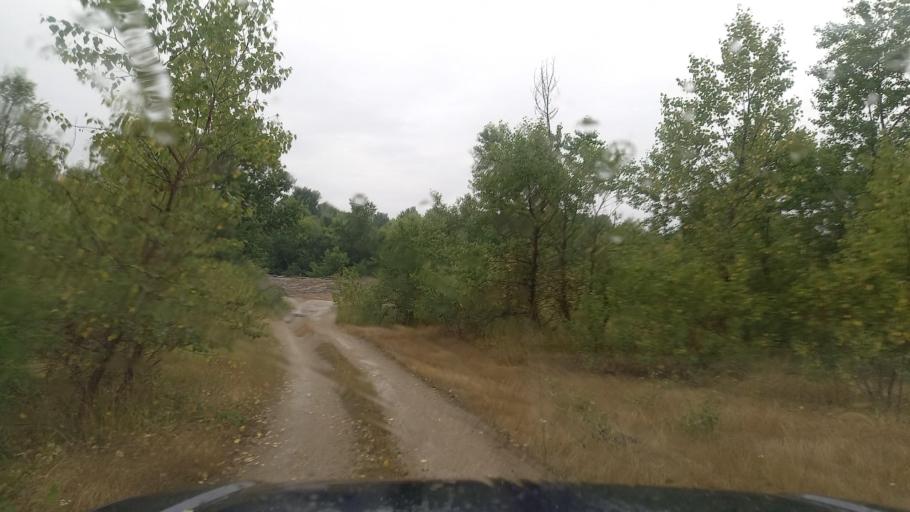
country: RU
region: Krasnodarskiy
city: Vasyurinskaya
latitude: 45.0346
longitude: 39.4714
